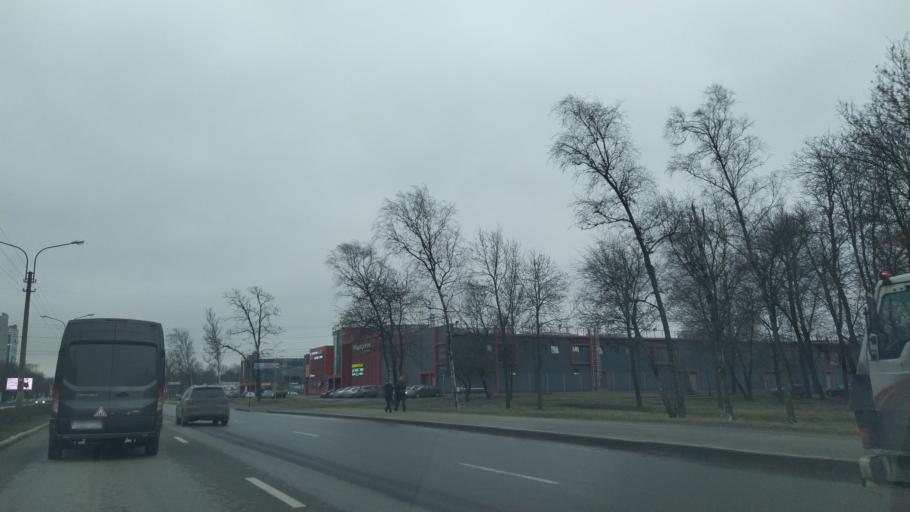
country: RU
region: St.-Petersburg
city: Kupchino
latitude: 59.8337
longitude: 30.3390
